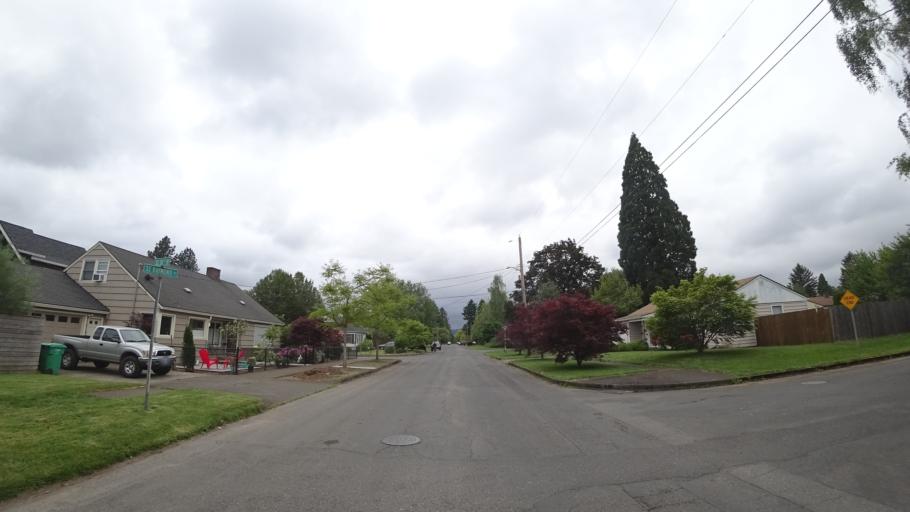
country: US
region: Oregon
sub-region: Multnomah County
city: Lents
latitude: 45.4866
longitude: -122.6109
